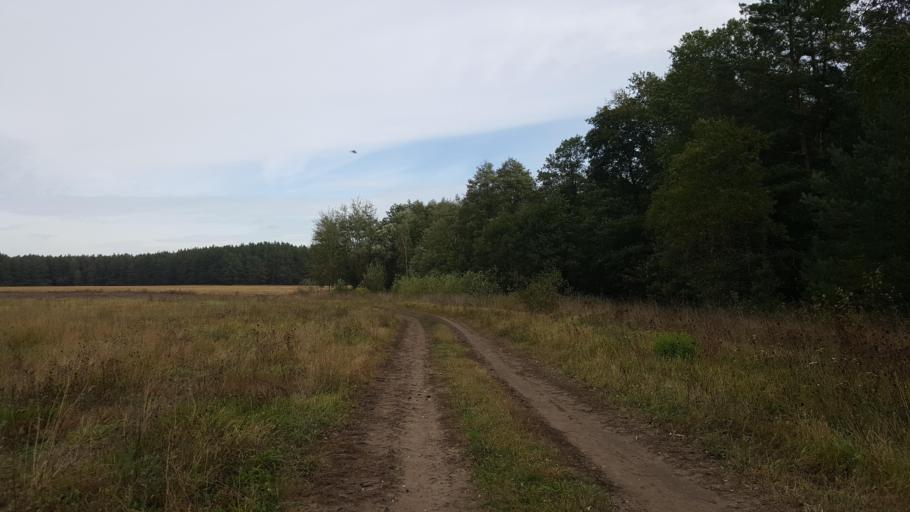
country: BY
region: Brest
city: Kamyanyets
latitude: 52.4231
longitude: 23.8945
